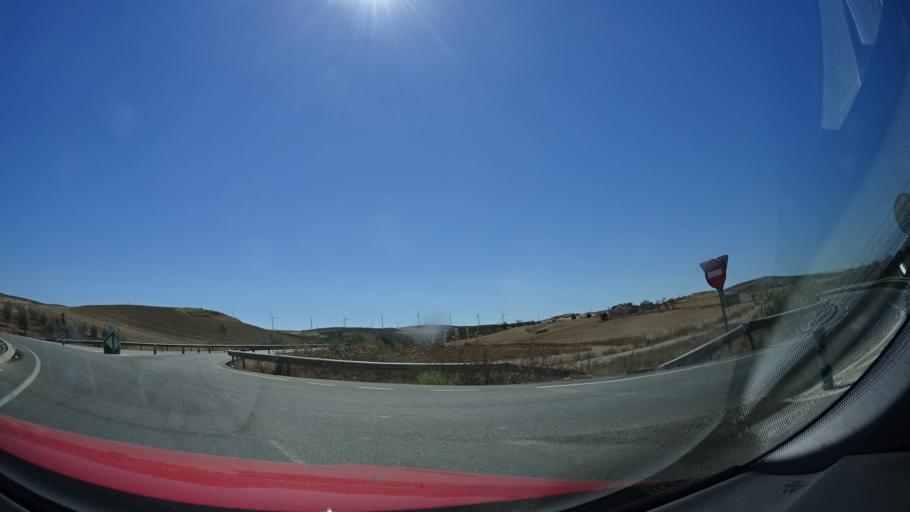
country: ES
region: Andalusia
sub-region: Provincia de Malaga
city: Sierra de Yeguas
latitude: 37.1244
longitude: -4.8768
